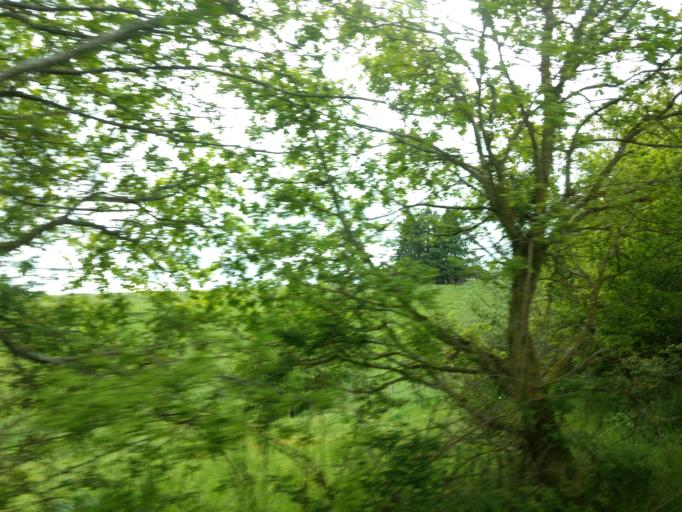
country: FR
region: Midi-Pyrenees
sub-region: Departement de l'Aveyron
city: Cassagnes-Begonhes
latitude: 44.1070
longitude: 2.6185
